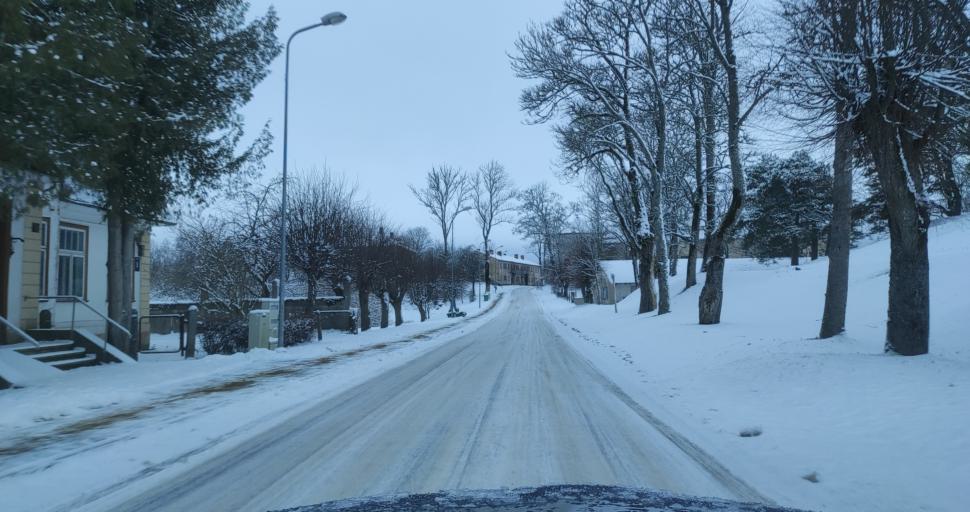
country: LV
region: Alsunga
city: Alsunga
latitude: 56.9804
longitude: 21.5692
